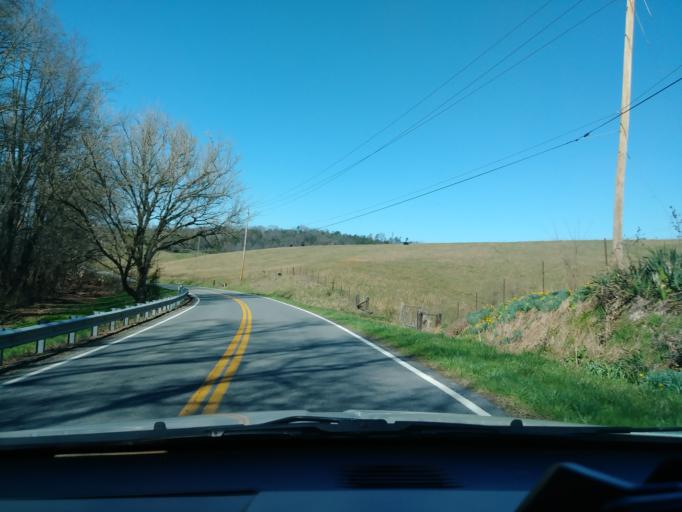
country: US
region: Tennessee
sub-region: Cocke County
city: Newport
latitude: 35.9949
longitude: -83.0721
